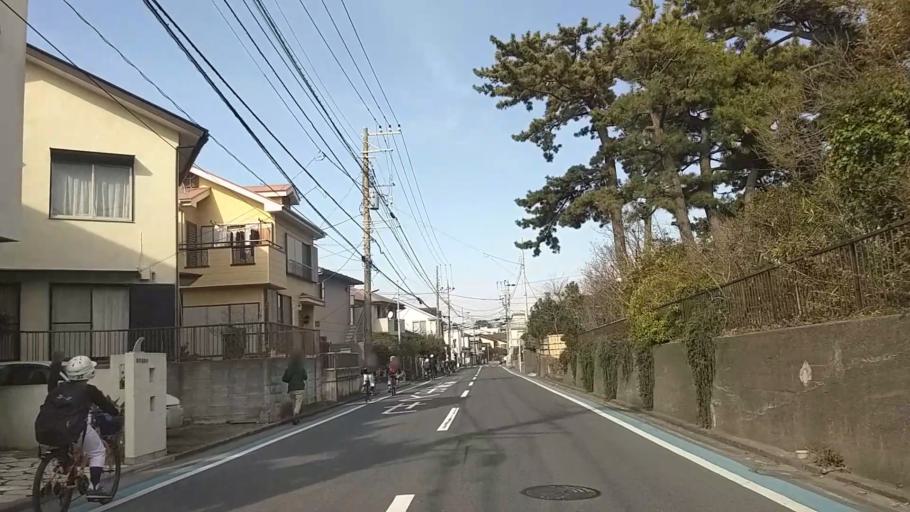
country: JP
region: Kanagawa
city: Chigasaki
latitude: 35.3201
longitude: 139.3998
